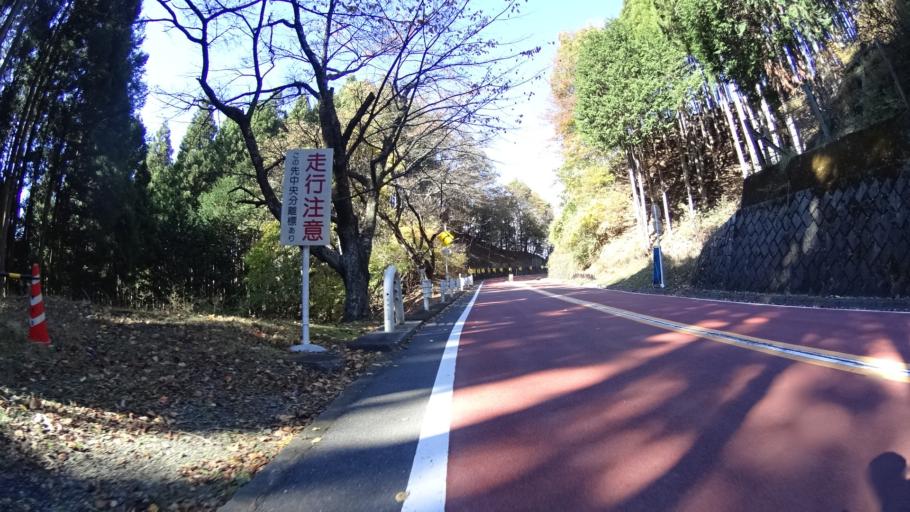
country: JP
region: Yamanashi
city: Uenohara
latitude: 35.7581
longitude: 139.0347
